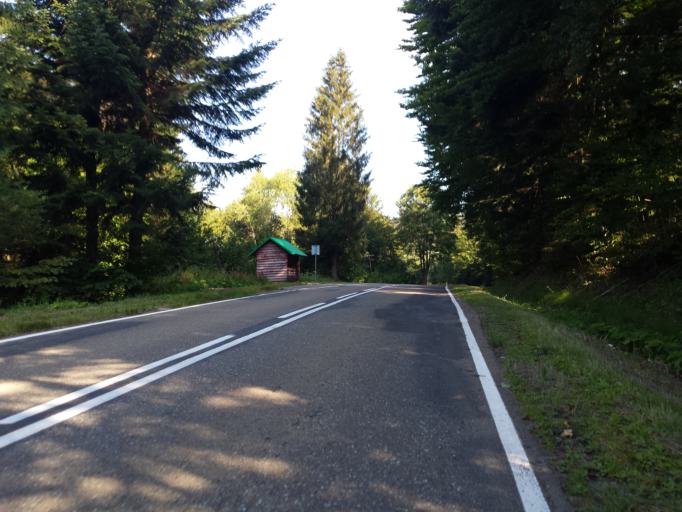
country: PL
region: Subcarpathian Voivodeship
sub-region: Powiat leski
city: Cisna
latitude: 49.2331
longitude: 22.3024
